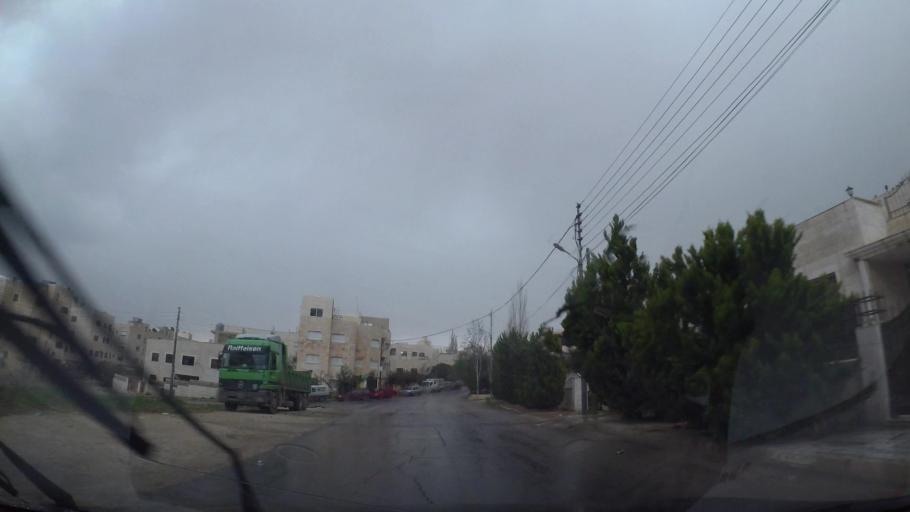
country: JO
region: Amman
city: Amman
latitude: 32.0052
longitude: 35.9587
